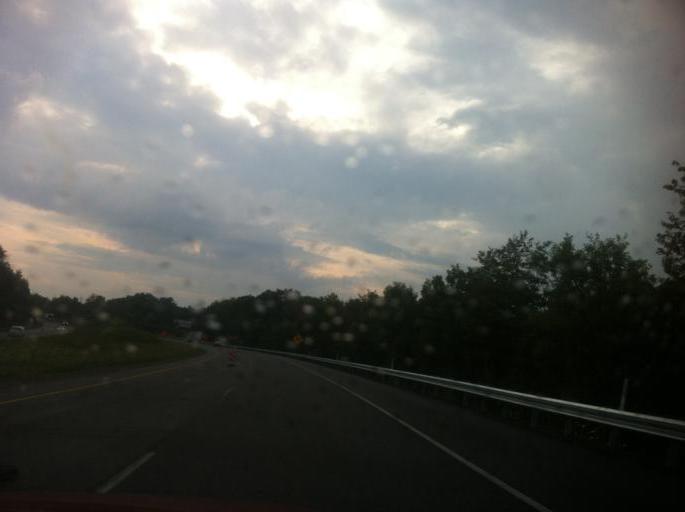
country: US
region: Pennsylvania
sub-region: Clarion County
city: Knox
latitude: 41.2004
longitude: -79.4881
